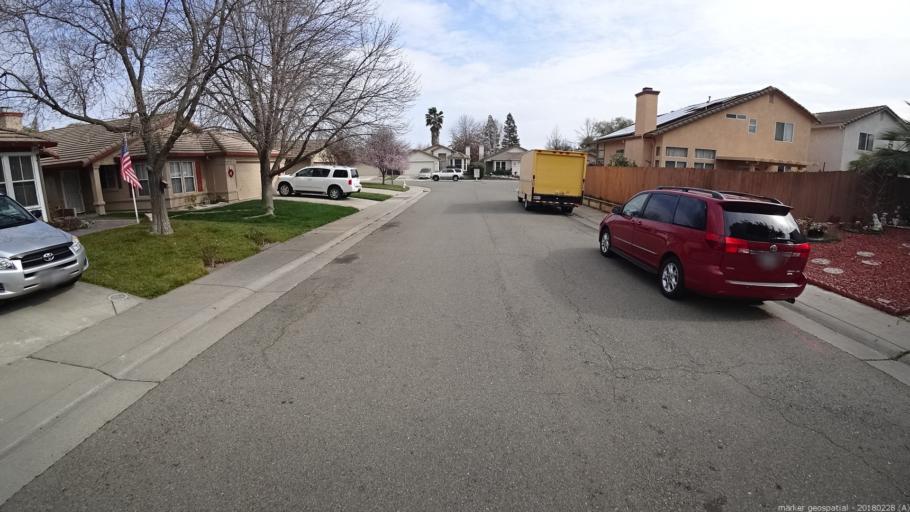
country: US
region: California
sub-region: Sacramento County
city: Antelope
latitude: 38.7091
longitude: -121.3249
